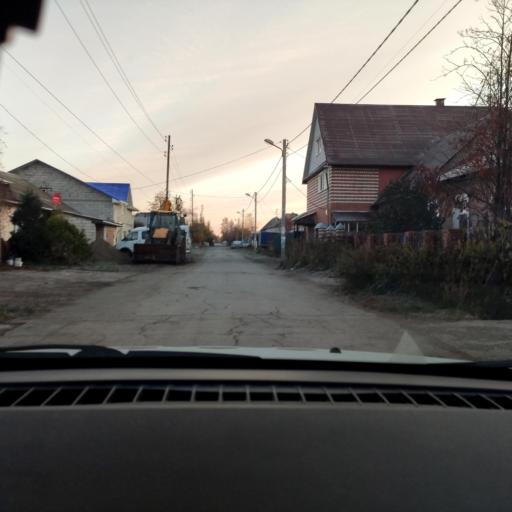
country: RU
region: Perm
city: Perm
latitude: 58.0534
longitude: 56.3585
